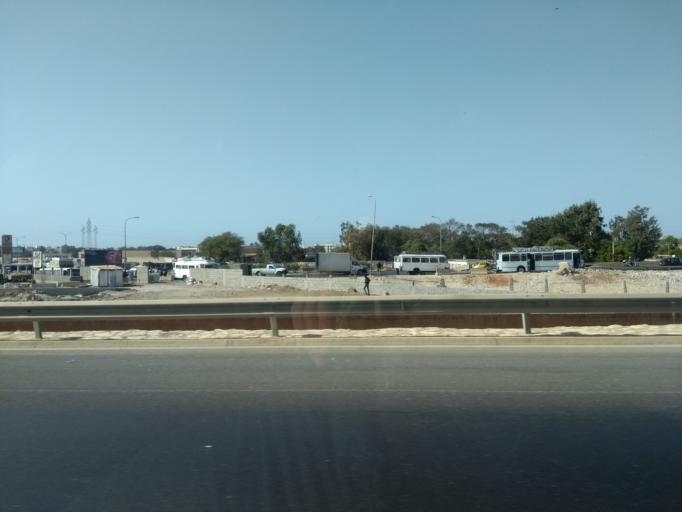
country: SN
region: Dakar
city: Pikine
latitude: 14.7429
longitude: -17.3978
